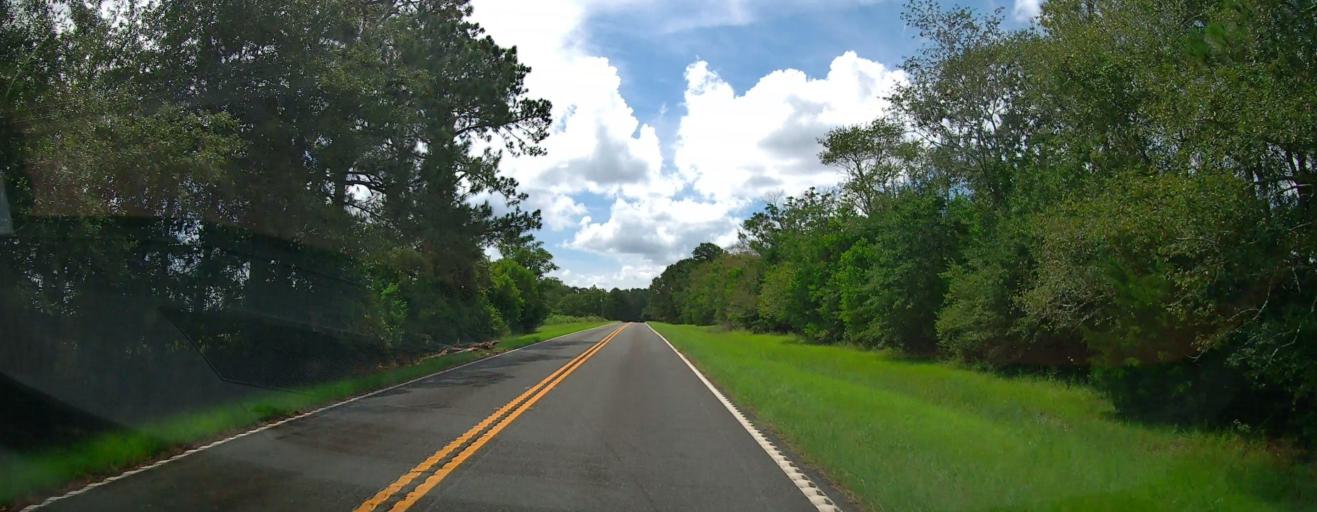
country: US
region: Georgia
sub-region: Taylor County
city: Reynolds
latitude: 32.4362
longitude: -84.1624
